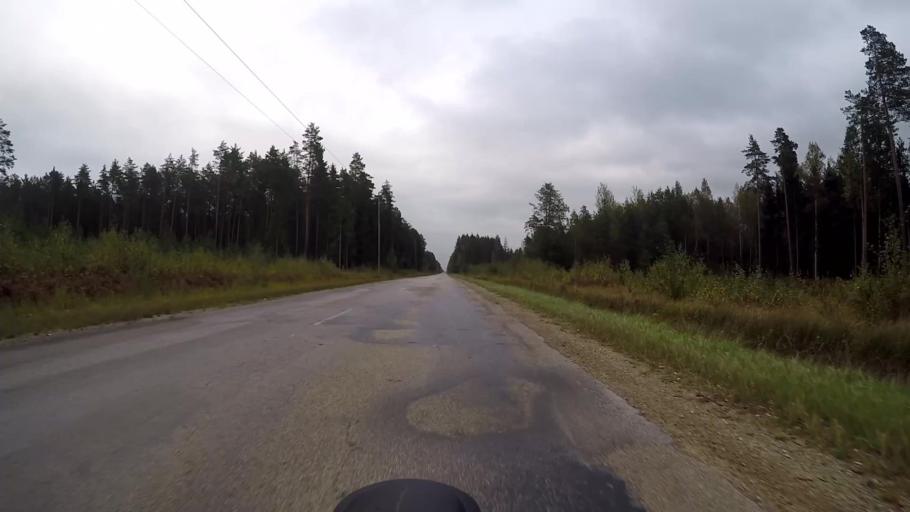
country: LV
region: Saulkrastu
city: Saulkrasti
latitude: 57.2702
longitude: 24.4661
